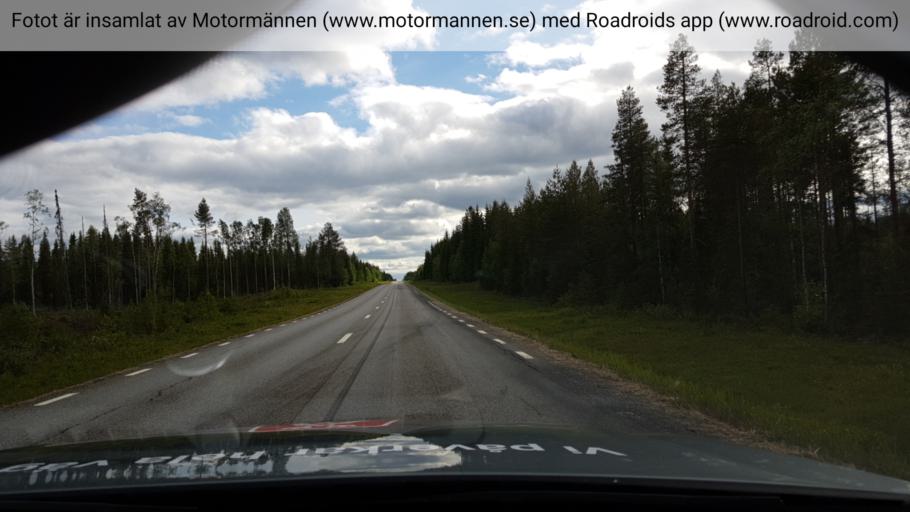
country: SE
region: Jaemtland
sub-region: Stroemsunds Kommun
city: Stroemsund
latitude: 63.7236
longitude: 15.4740
